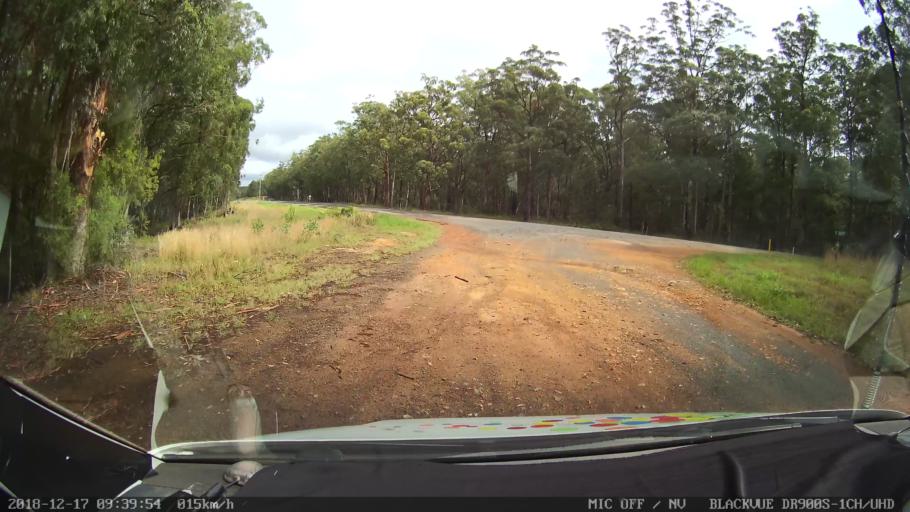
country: AU
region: New South Wales
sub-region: Tenterfield Municipality
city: Carrolls Creek
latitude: -28.9261
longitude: 152.3162
